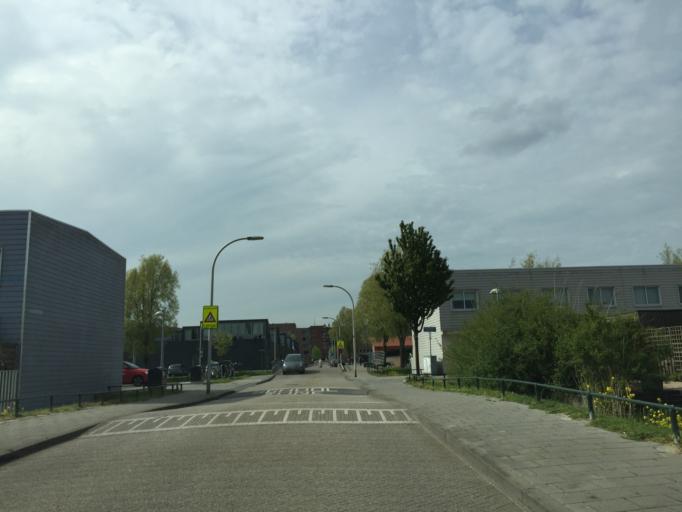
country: NL
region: South Holland
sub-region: Gemeente Den Haag
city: Ypenburg
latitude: 52.0368
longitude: 4.3718
